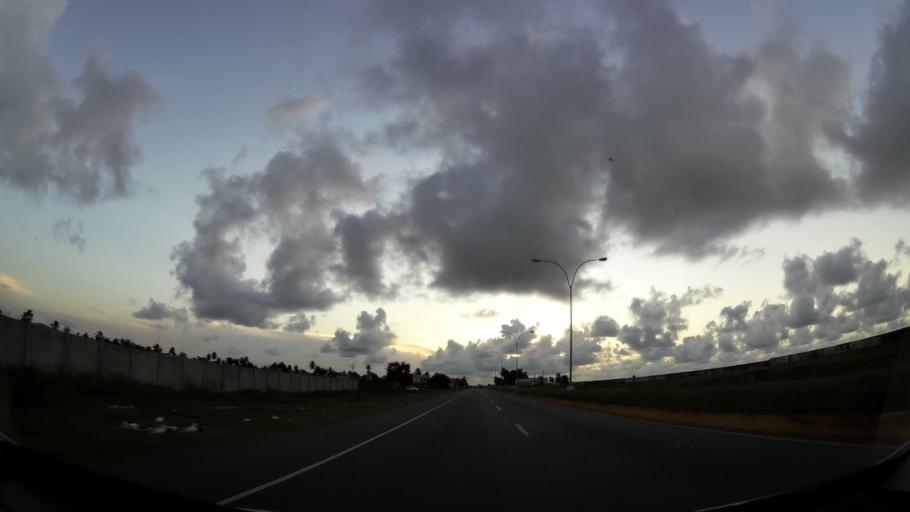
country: GY
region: Demerara-Mahaica
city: Georgetown
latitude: 6.8255
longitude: -58.1169
